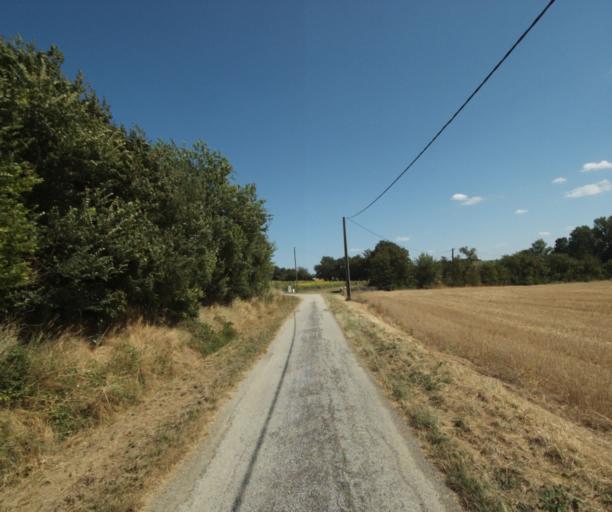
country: FR
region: Midi-Pyrenees
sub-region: Departement de la Haute-Garonne
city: Saint-Felix-Lauragais
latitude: 43.4849
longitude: 1.8981
